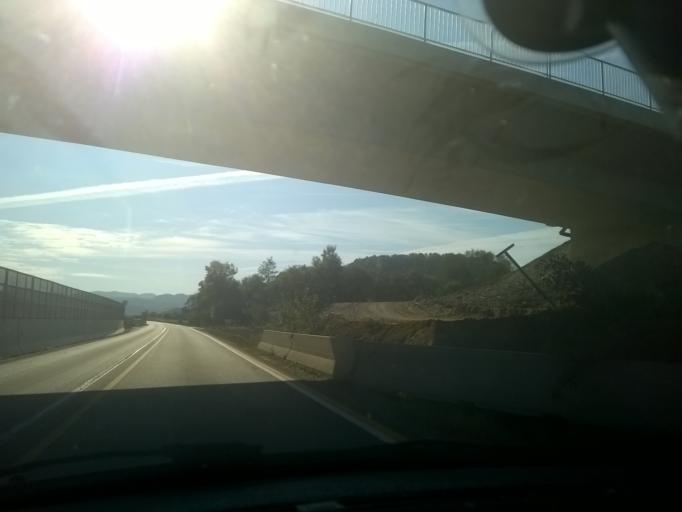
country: SI
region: Podlehnik
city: Podlehnik
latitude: 46.3485
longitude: 15.8691
